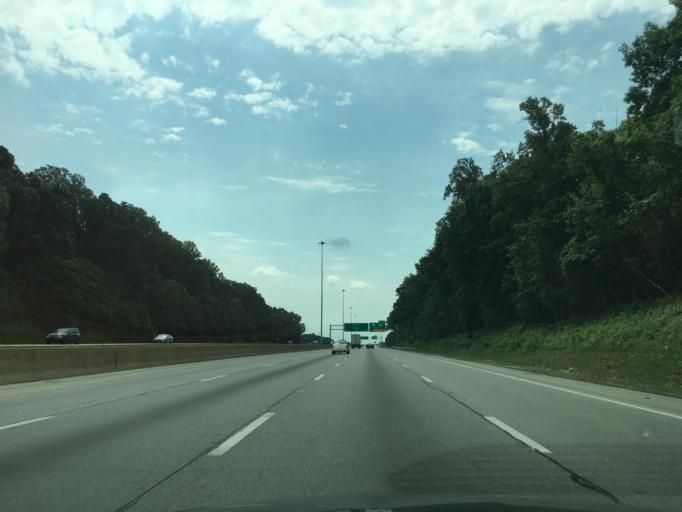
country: US
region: Ohio
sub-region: Summit County
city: Green
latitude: 40.9709
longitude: -81.4714
